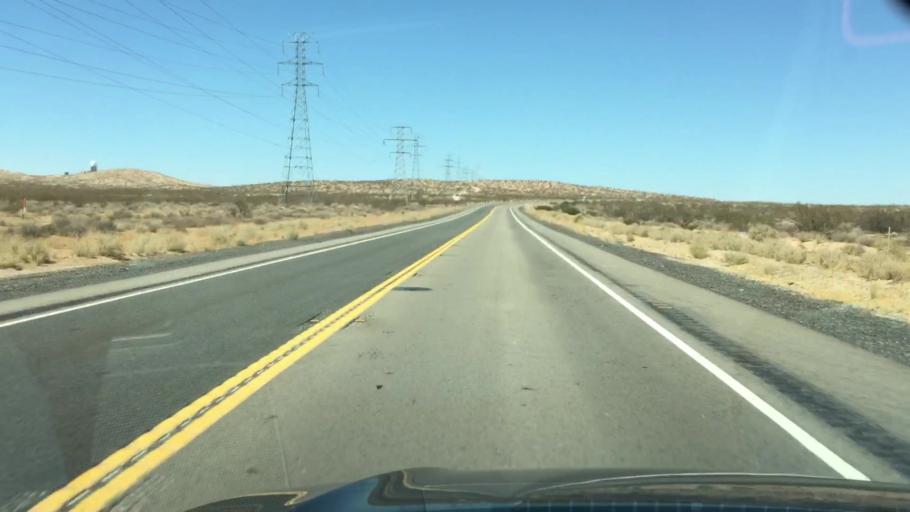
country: US
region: California
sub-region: Kern County
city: Boron
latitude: 35.0571
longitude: -117.5596
